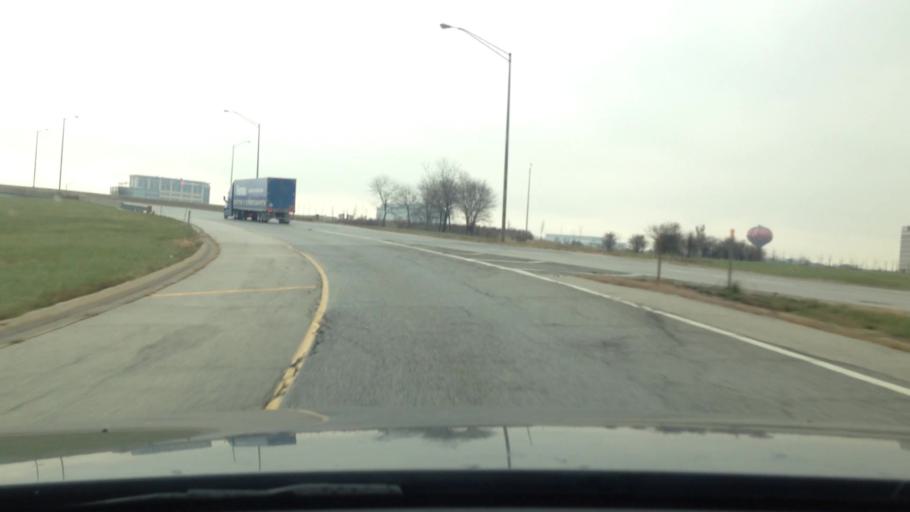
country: US
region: Illinois
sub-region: Cook County
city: Rosemont
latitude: 41.9861
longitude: -87.8670
